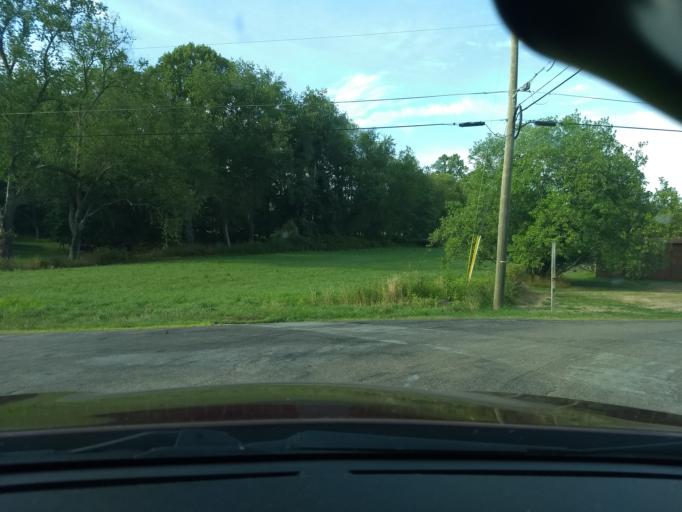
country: US
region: Pennsylvania
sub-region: Armstrong County
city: Freeport
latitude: 40.6666
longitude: -79.6632
